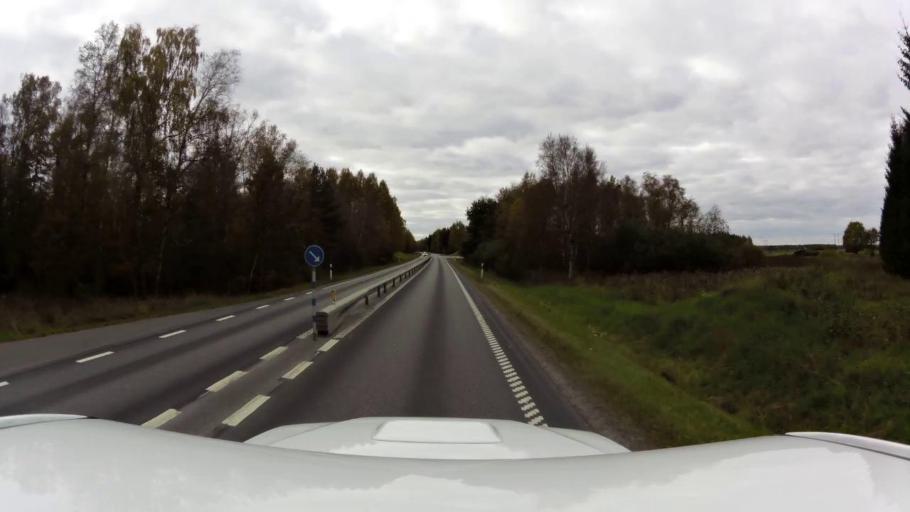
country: SE
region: OEstergoetland
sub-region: Linkopings Kommun
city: Malmslatt
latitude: 58.3853
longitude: 15.5423
